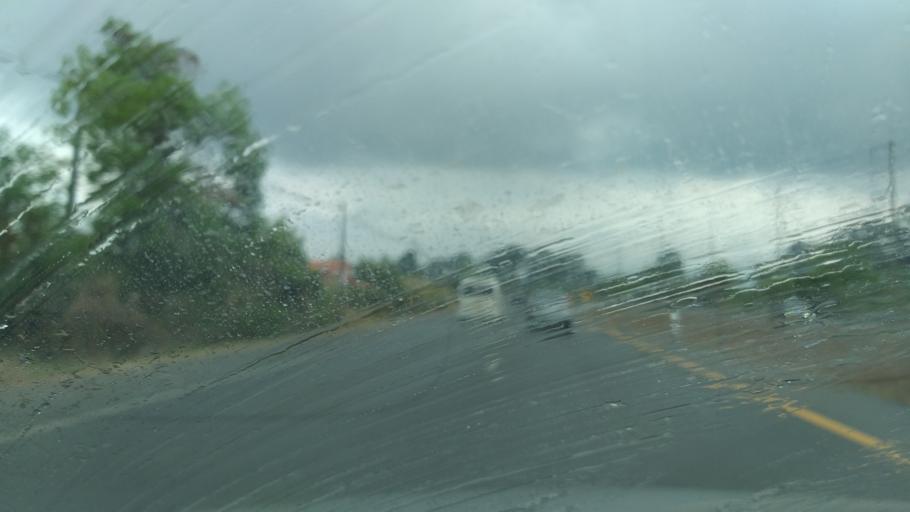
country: TH
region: Chanthaburi
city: Khlung
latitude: 12.4565
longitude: 102.2712
